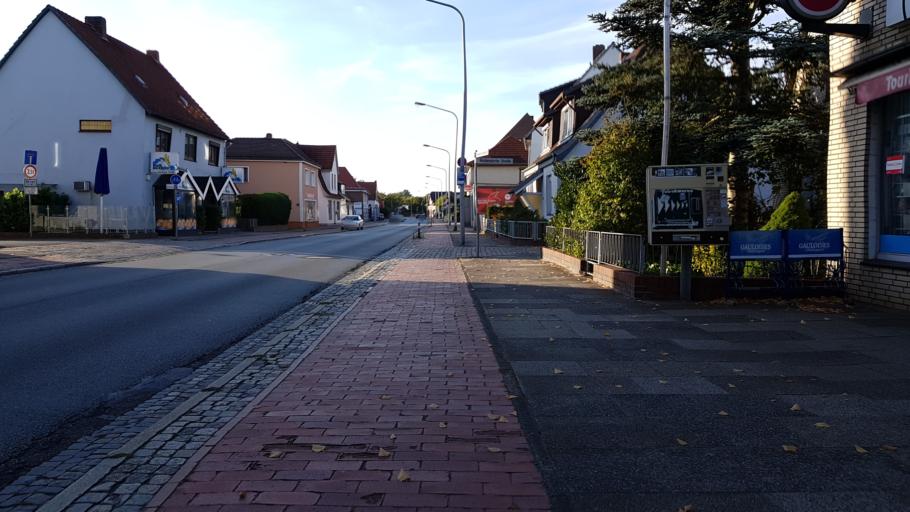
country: DE
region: Lower Saxony
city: Riede
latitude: 53.0363
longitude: 8.9483
